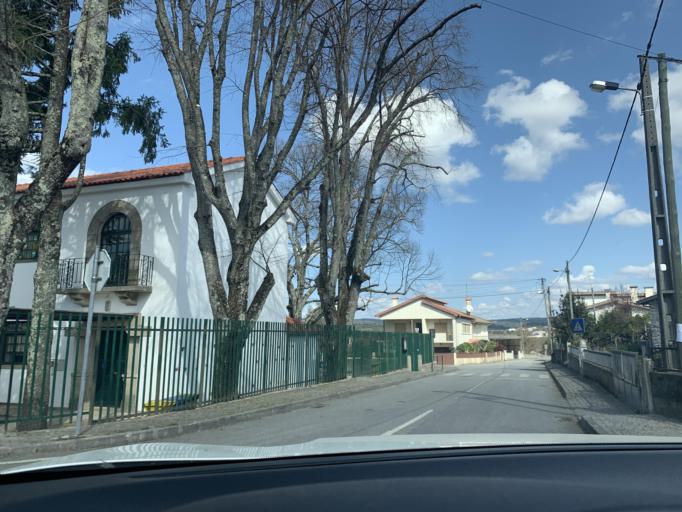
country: PT
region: Viseu
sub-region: Viseu
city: Rio de Loba
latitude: 40.6720
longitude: -7.8818
